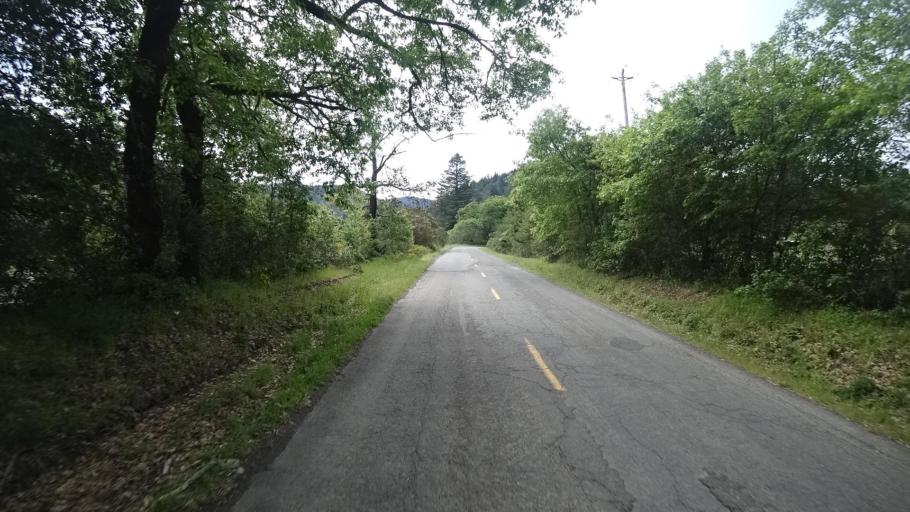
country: US
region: California
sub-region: Humboldt County
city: Redway
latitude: 40.0706
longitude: -123.8283
